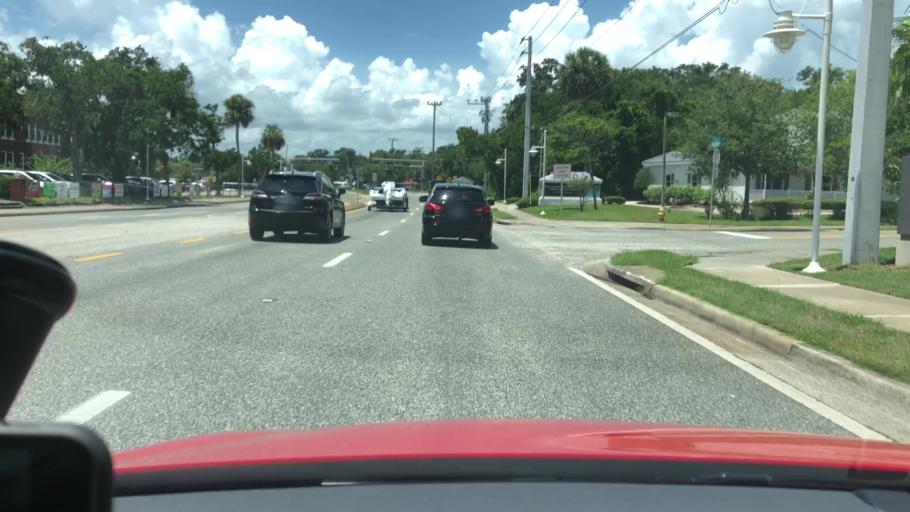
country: US
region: Florida
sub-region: Volusia County
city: Port Orange
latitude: 29.1468
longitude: -80.9966
